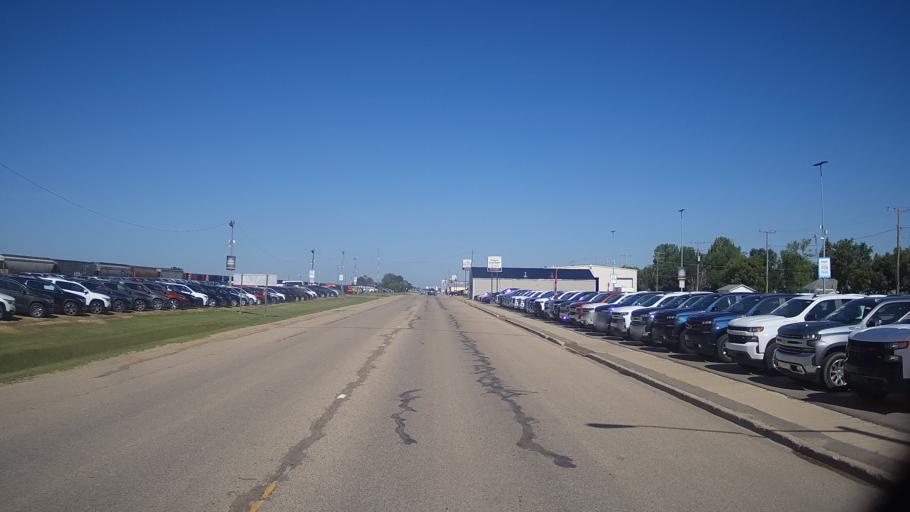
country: CA
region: Saskatchewan
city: Watrous
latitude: 51.6697
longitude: -105.4625
